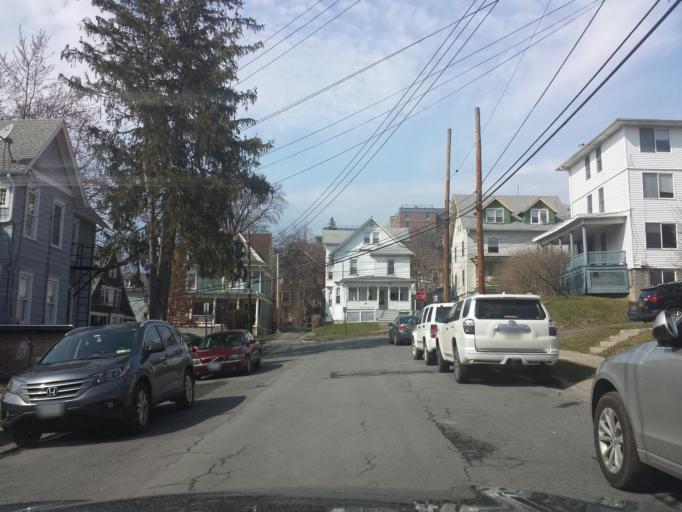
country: US
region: New York
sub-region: Tompkins County
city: East Ithaca
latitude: 42.4392
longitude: -76.4859
